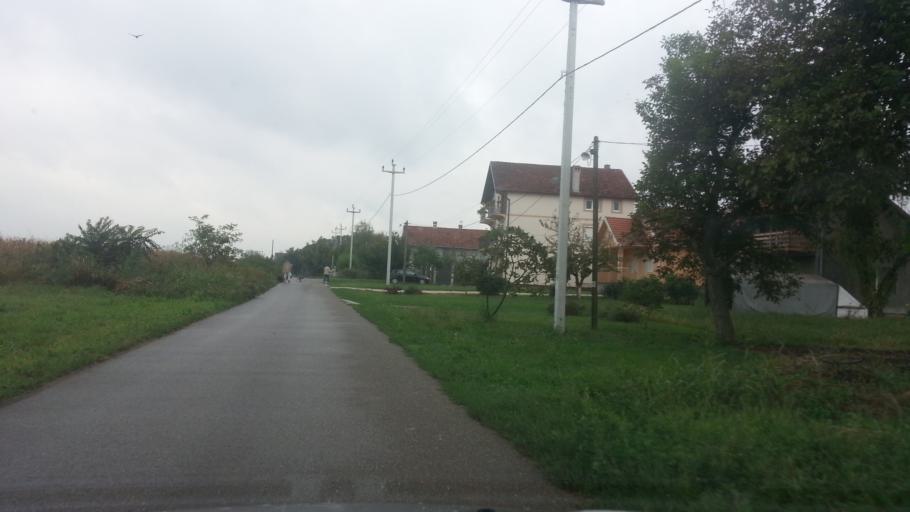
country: RS
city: Novi Banovci
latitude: 44.9405
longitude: 20.2943
